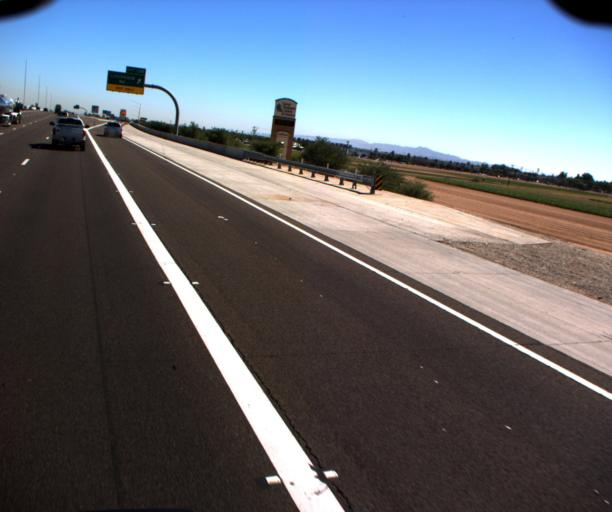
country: US
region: Arizona
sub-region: Maricopa County
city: Goodyear
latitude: 33.4578
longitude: -112.3647
